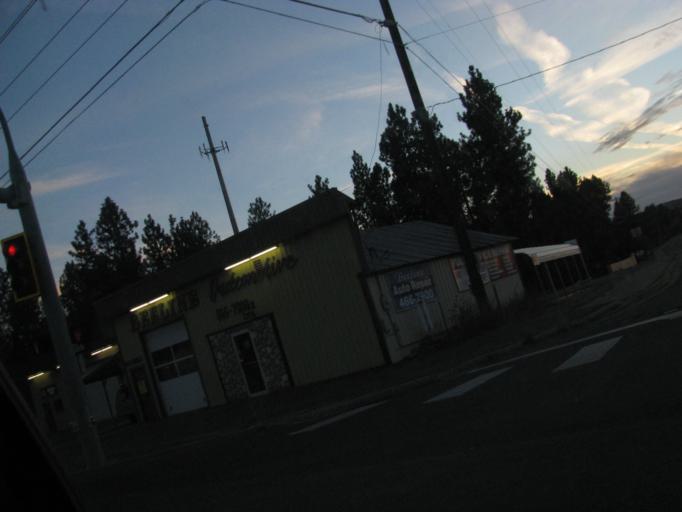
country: US
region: Washington
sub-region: Spokane County
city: Mead
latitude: 47.8019
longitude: -117.3490
